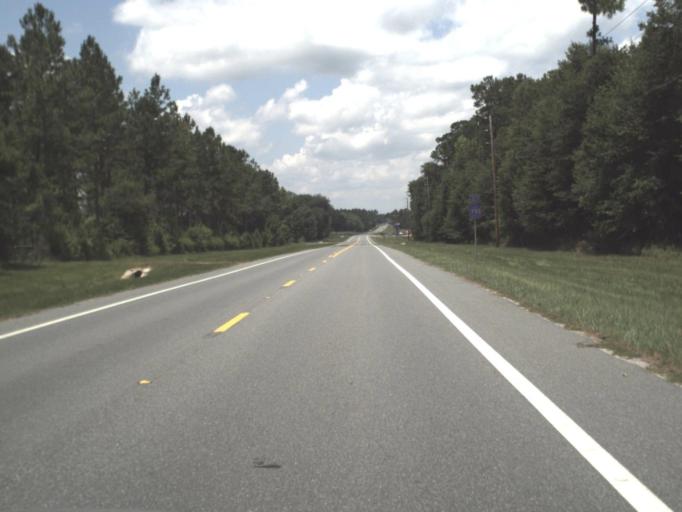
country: US
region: Florida
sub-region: Union County
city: Lake Butler
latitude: 30.0025
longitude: -82.5234
